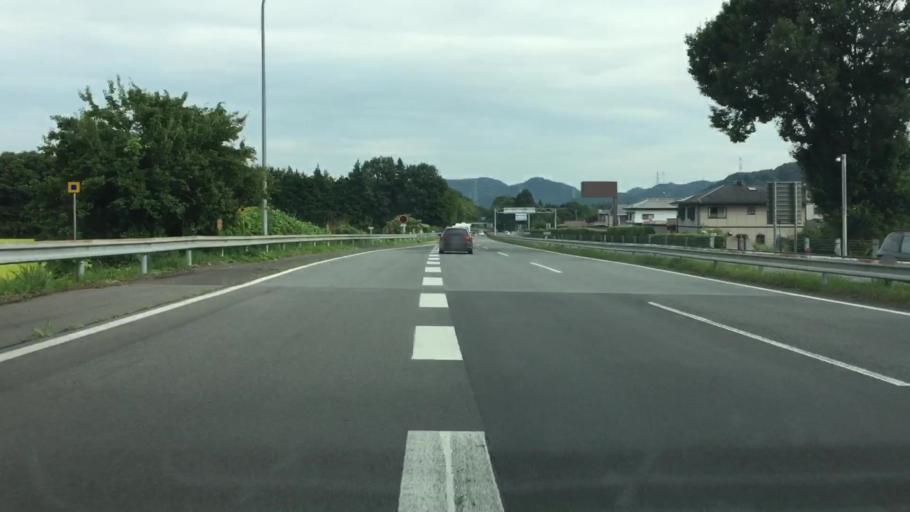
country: JP
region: Tochigi
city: Imaichi
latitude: 36.6850
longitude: 139.7579
